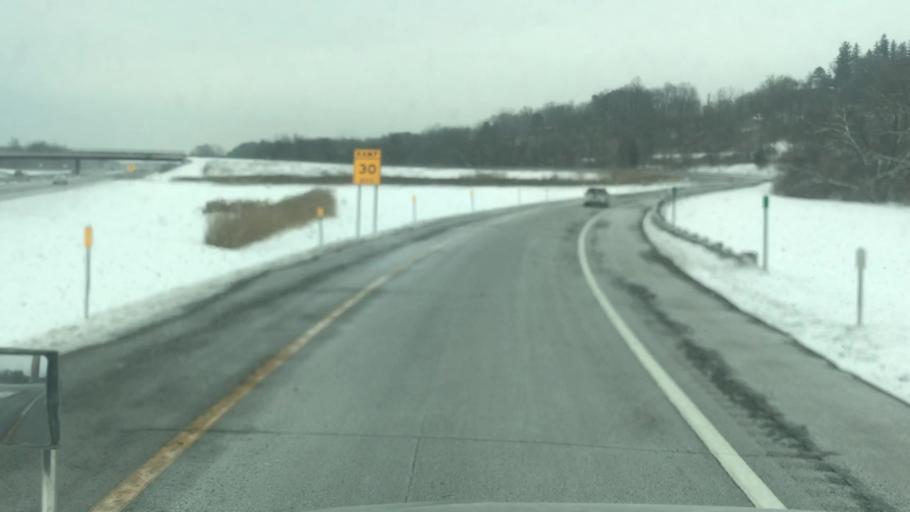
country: US
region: New York
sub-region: Montgomery County
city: Fonda
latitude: 42.9453
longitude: -74.3634
